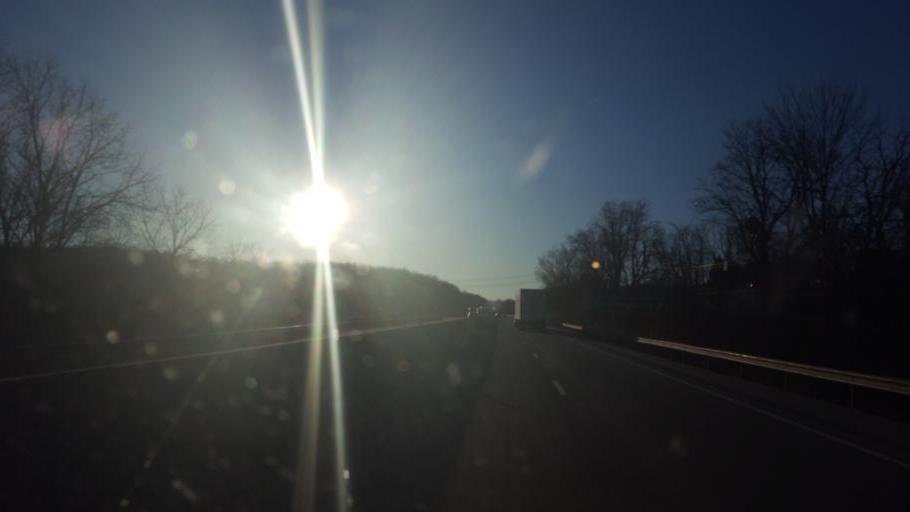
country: US
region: Pennsylvania
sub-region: Washington County
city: Ellsworth
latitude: 40.1661
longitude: -80.0787
